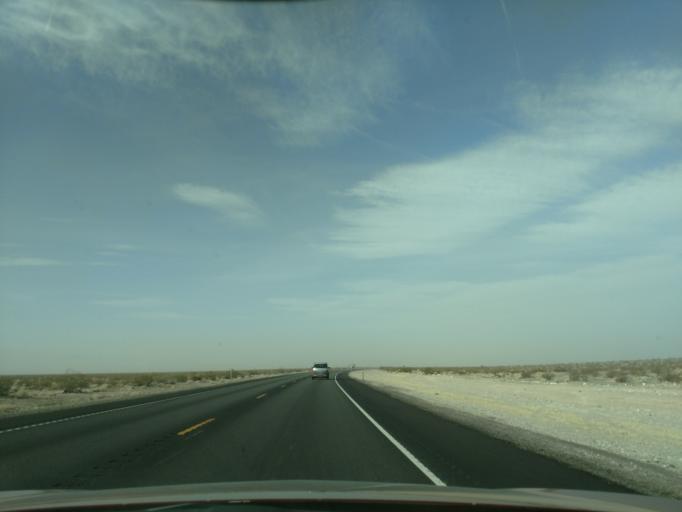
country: US
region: Nevada
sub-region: Nye County
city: Beatty
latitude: 36.6318
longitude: -116.3504
